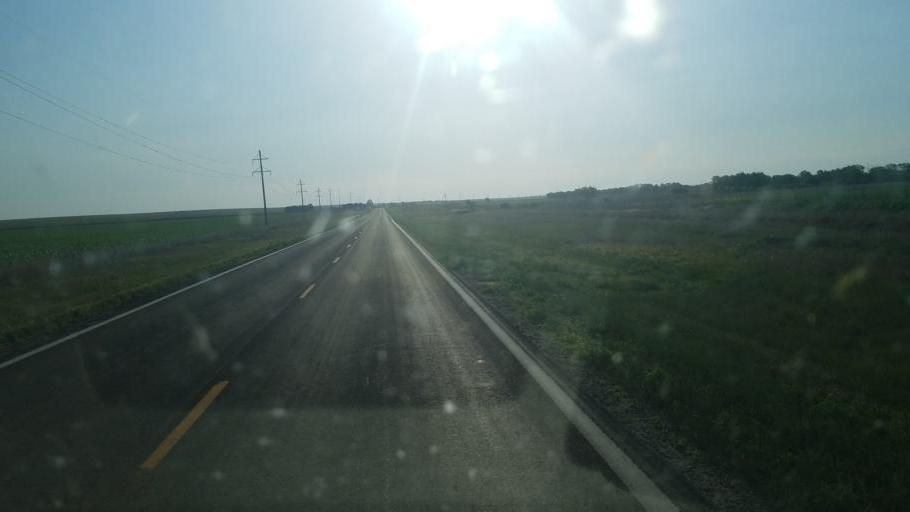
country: US
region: Kansas
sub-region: Hodgeman County
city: Jetmore
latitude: 38.0907
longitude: -99.8223
